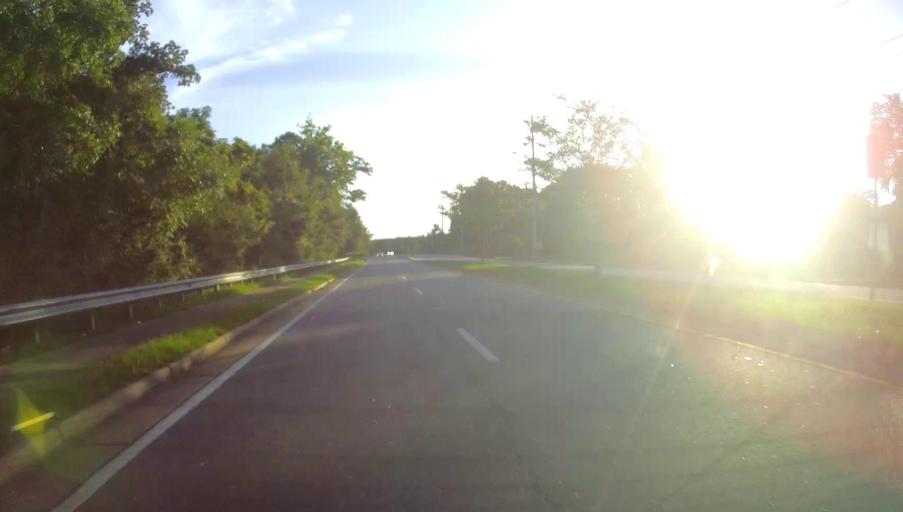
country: US
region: Georgia
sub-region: Muscogee County
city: Columbus
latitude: 32.5188
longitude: -84.8786
